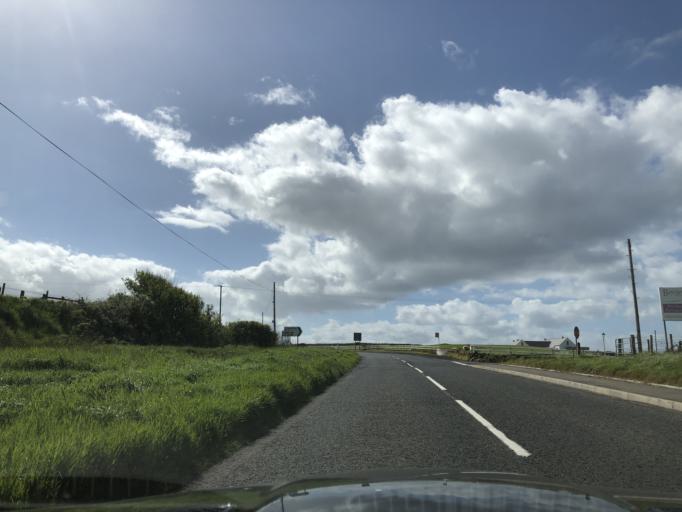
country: GB
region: Northern Ireland
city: Bushmills
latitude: 55.2133
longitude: -6.5624
